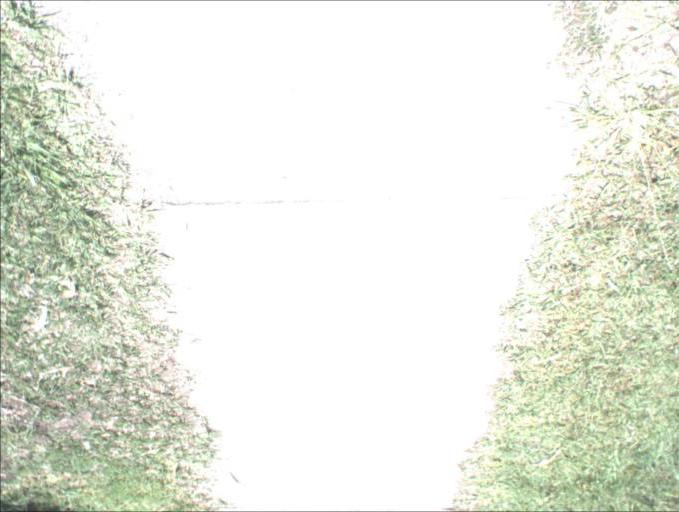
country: AU
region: Queensland
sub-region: Logan
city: Logan City
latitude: -27.6354
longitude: 153.1125
